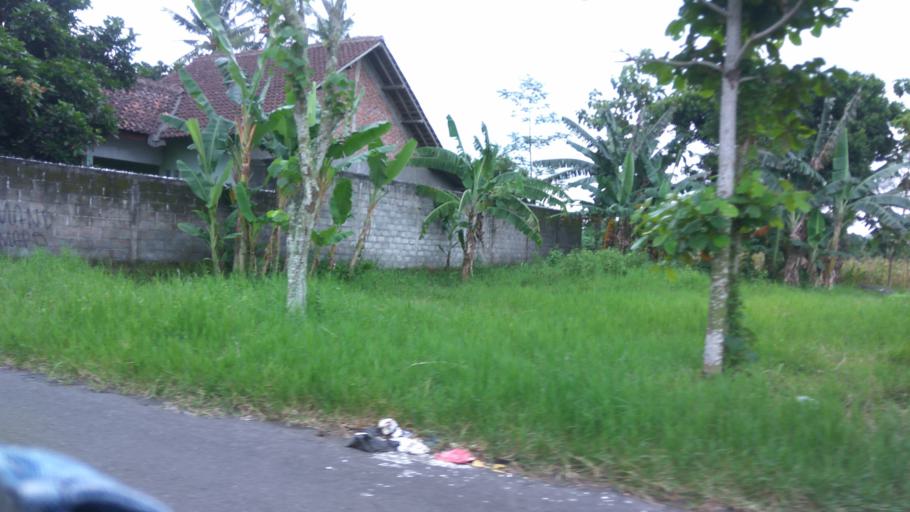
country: ID
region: Daerah Istimewa Yogyakarta
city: Melati
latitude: -7.7272
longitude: 110.4036
